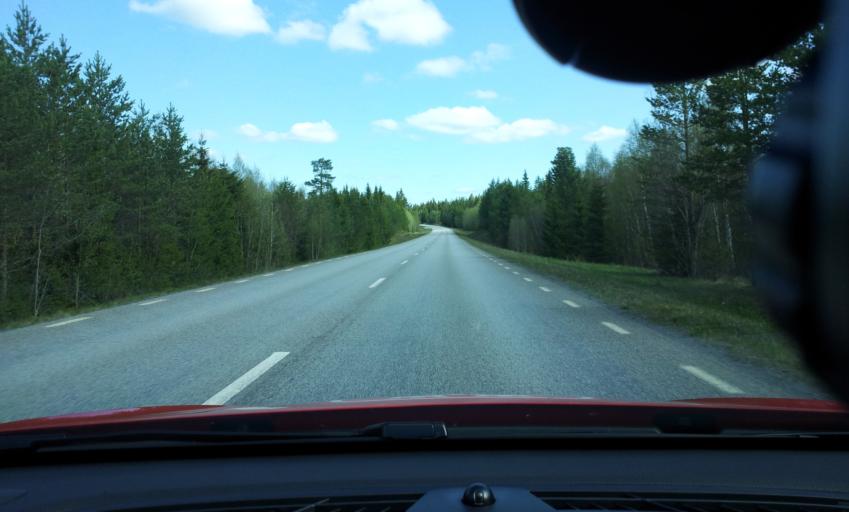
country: SE
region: Jaemtland
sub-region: Krokoms Kommun
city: Valla
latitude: 63.2930
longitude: 13.9267
